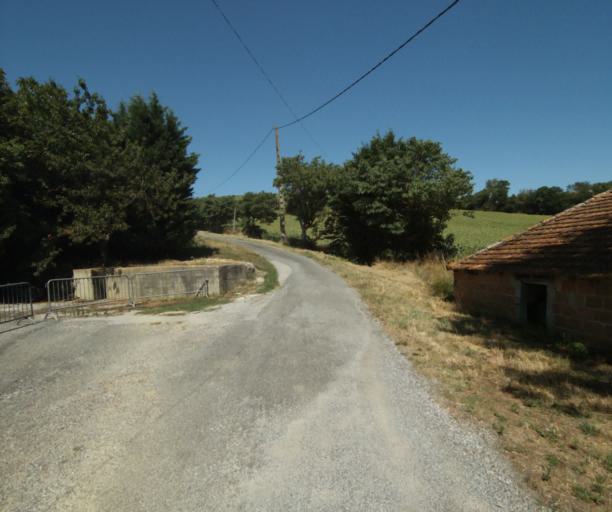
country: FR
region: Midi-Pyrenees
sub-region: Departement de la Haute-Garonne
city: Saint-Felix-Lauragais
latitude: 43.4980
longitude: 1.8801
